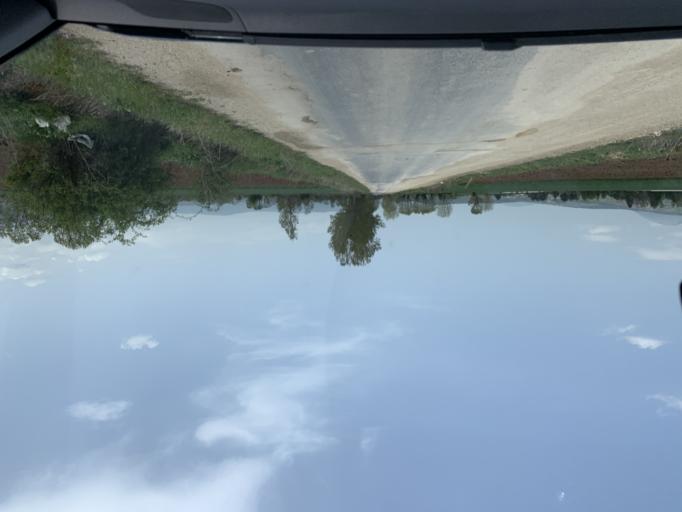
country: TR
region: Bolu
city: Bolu
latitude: 40.7470
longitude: 31.6624
